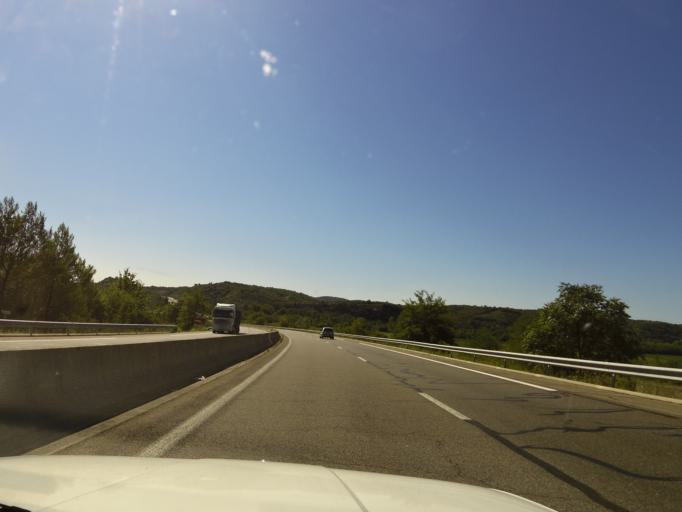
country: FR
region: Languedoc-Roussillon
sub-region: Departement du Gard
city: Vezenobres
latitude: 44.0215
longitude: 4.1472
